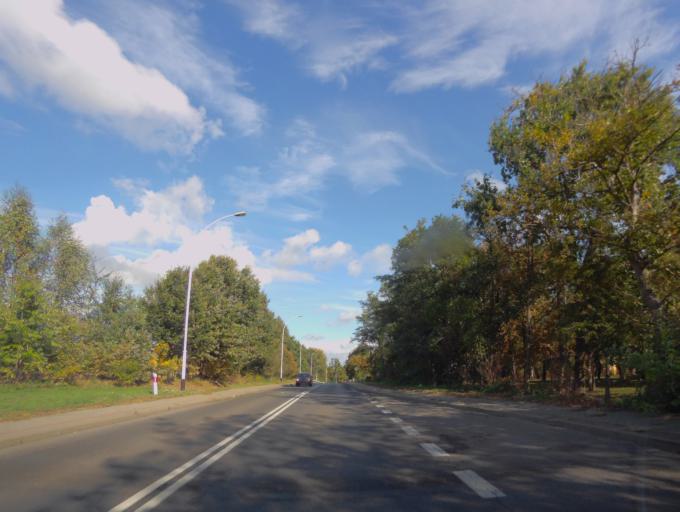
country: PL
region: Subcarpathian Voivodeship
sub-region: Powiat lezajski
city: Lezajsk
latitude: 50.2458
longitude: 22.4138
